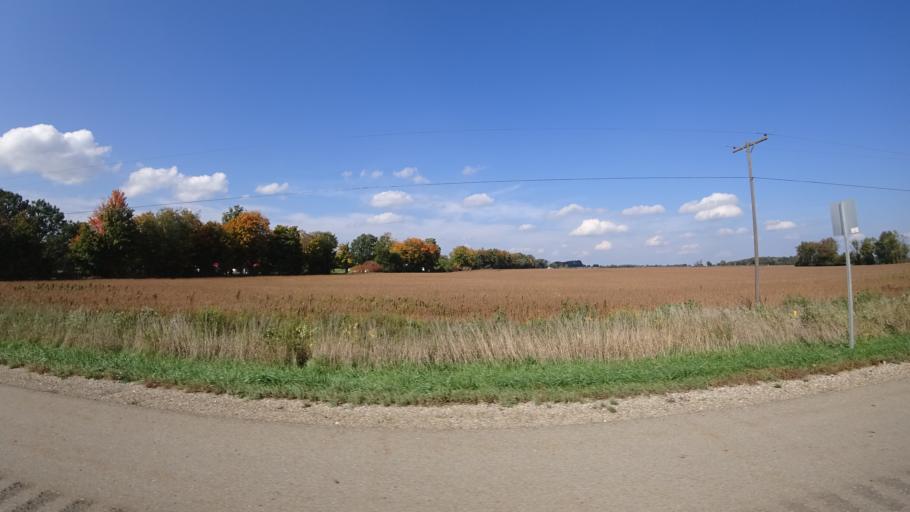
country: US
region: Michigan
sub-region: Jackson County
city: Concord
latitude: 42.1865
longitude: -84.6340
